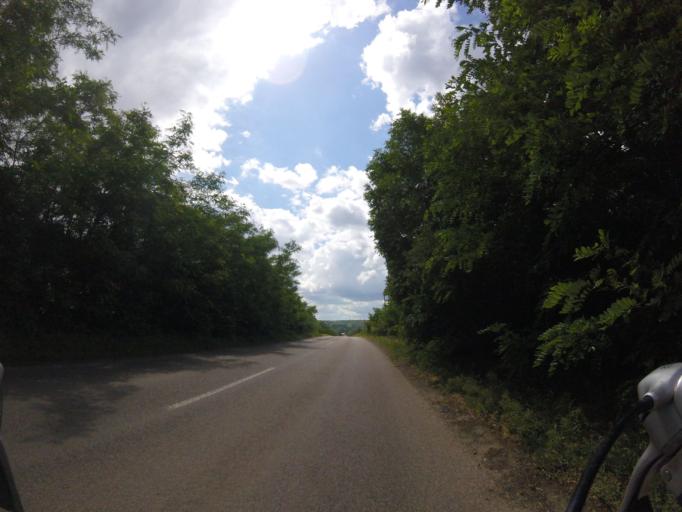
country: HU
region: Heves
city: Domoszlo
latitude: 47.8271
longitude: 20.0785
